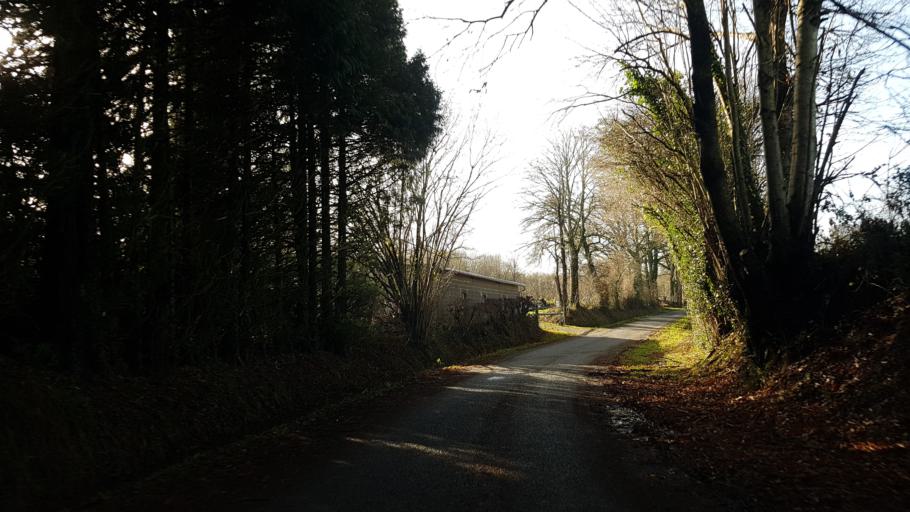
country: FR
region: Poitou-Charentes
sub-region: Departement de la Charente
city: Brigueuil
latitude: 45.9196
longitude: 0.8248
